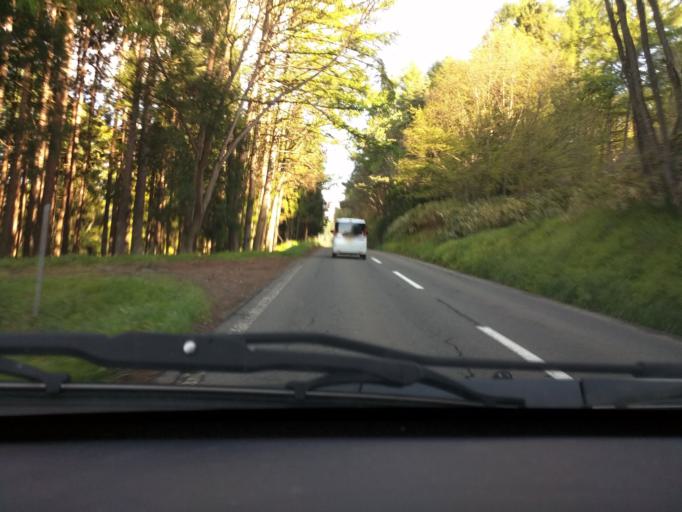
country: JP
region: Nagano
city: Nagano-shi
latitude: 36.6850
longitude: 138.1604
